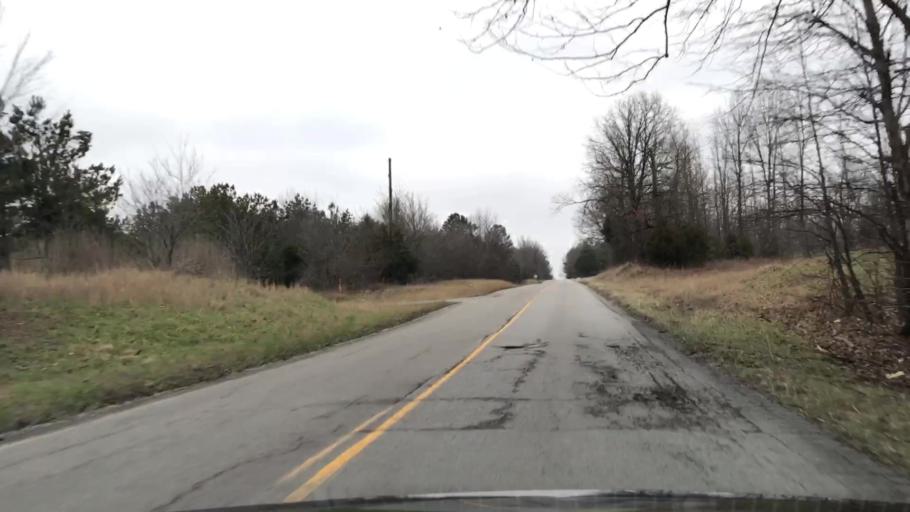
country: US
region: Kentucky
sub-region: Muhlenberg County
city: Morehead
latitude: 37.2796
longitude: -87.2088
